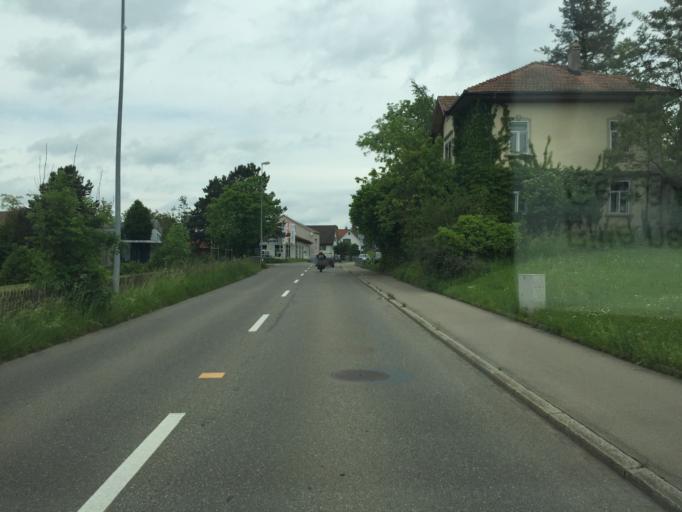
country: CH
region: Thurgau
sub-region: Frauenfeld District
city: Steckborn
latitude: 47.6609
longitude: 8.9734
